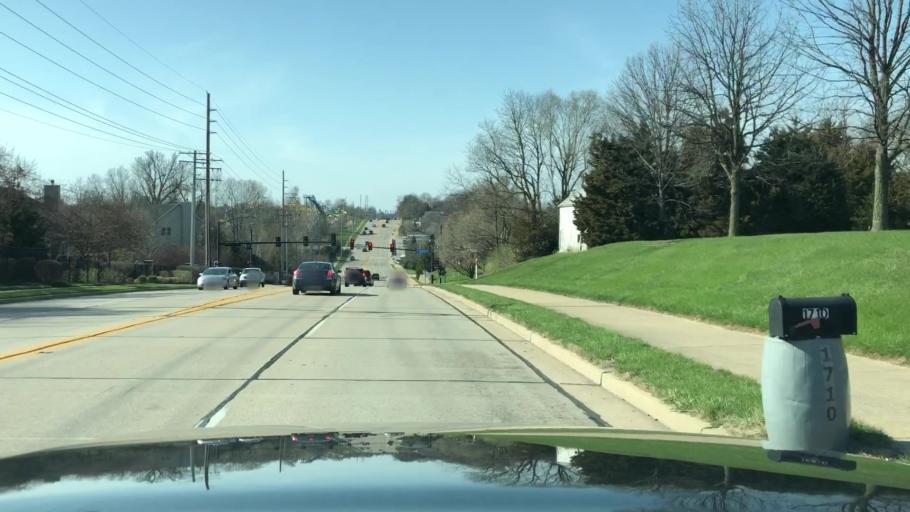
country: US
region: Missouri
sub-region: Saint Charles County
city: Saint Charles
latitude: 38.7640
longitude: -90.5428
